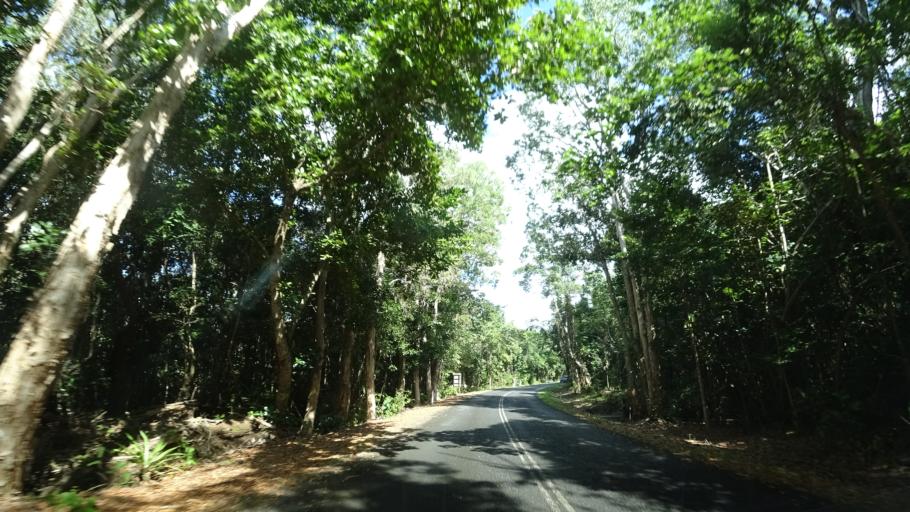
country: AU
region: Queensland
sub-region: Cairns
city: Port Douglas
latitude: -16.1748
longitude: 145.4399
